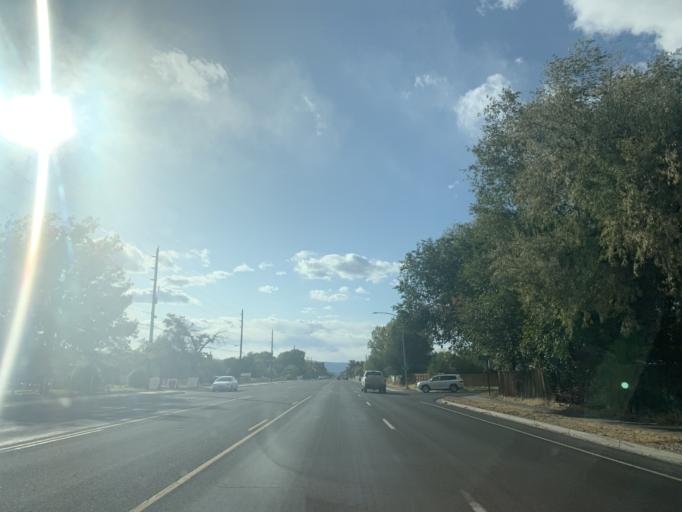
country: US
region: Colorado
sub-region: Mesa County
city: Fruitvale
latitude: 39.0918
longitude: -108.4825
